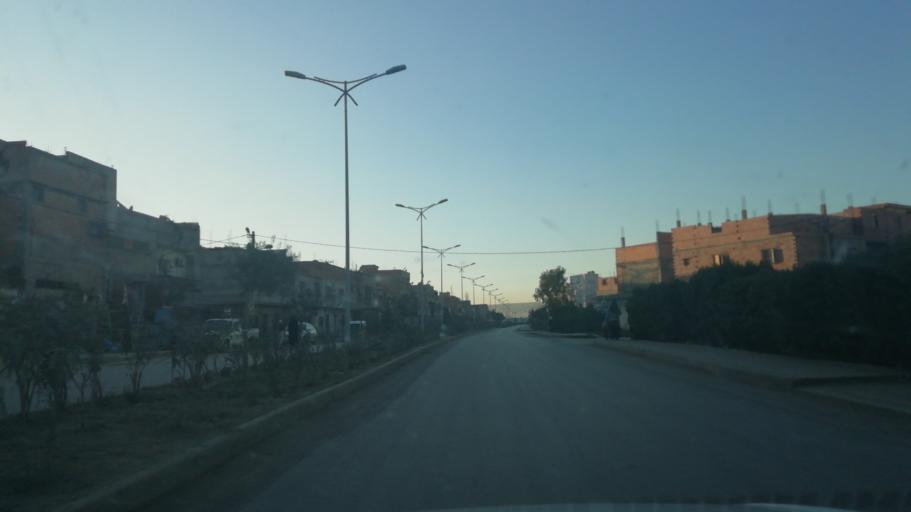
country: DZ
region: Oran
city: Es Senia
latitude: 35.6488
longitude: -0.5741
